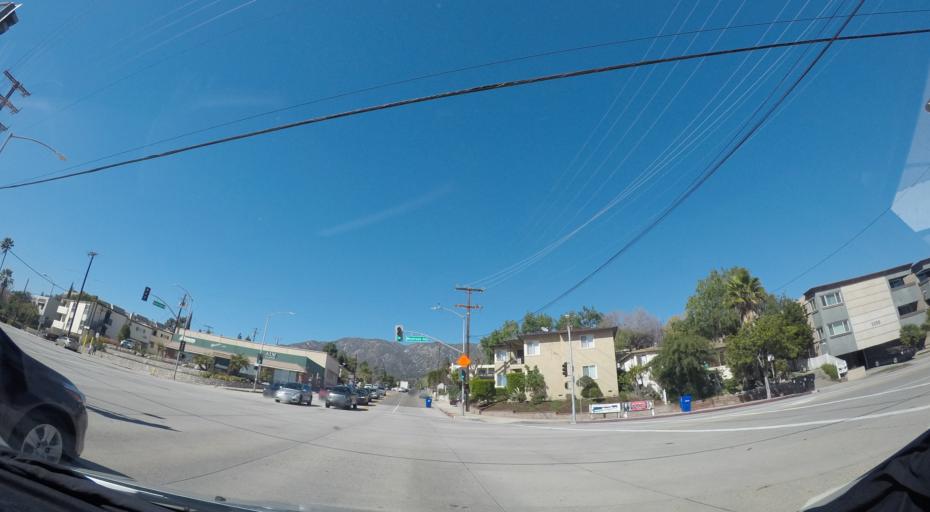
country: US
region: California
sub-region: Los Angeles County
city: La Crescenta-Montrose
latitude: 34.2091
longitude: -118.2279
